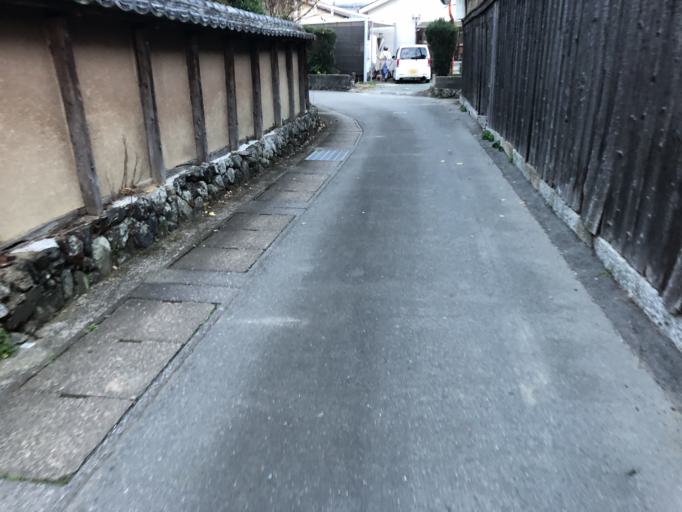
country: JP
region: Kyoto
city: Kameoka
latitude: 35.0574
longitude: 135.5619
